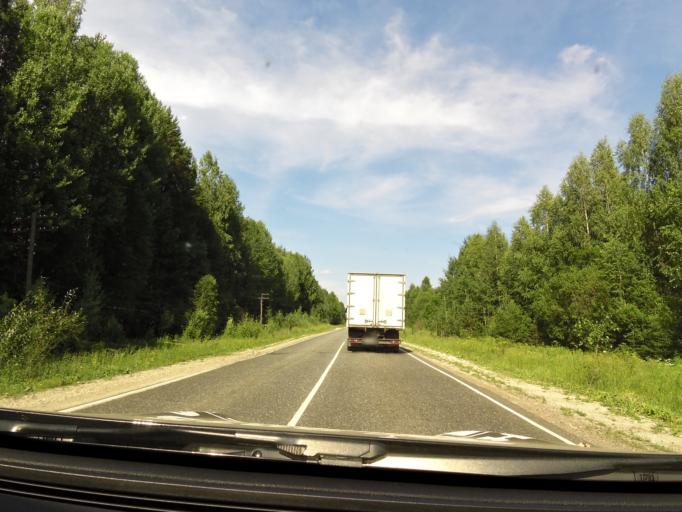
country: RU
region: Kirov
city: Belaya Kholunitsa
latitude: 58.7951
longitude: 50.5244
